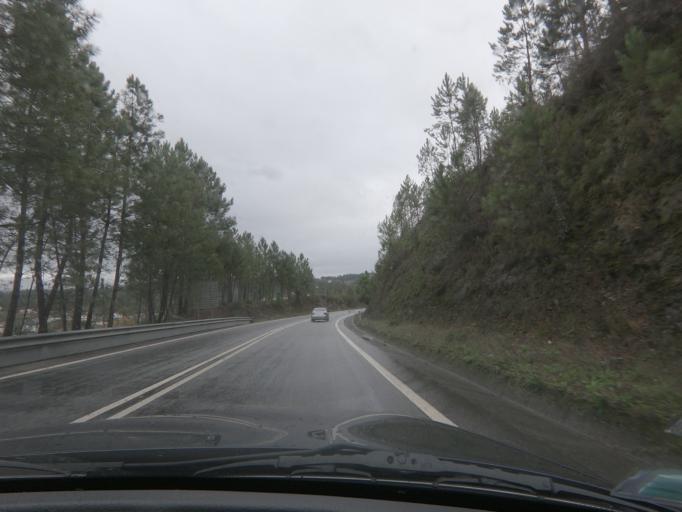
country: PT
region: Porto
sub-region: Amarante
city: Teloes
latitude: 41.3235
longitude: -8.0627
